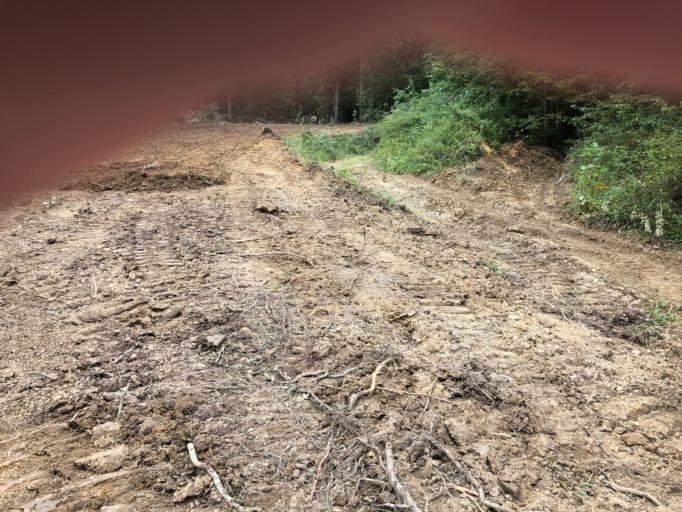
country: US
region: Tennessee
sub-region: Fentress County
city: Jamestown
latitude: 36.3153
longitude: -84.8561
